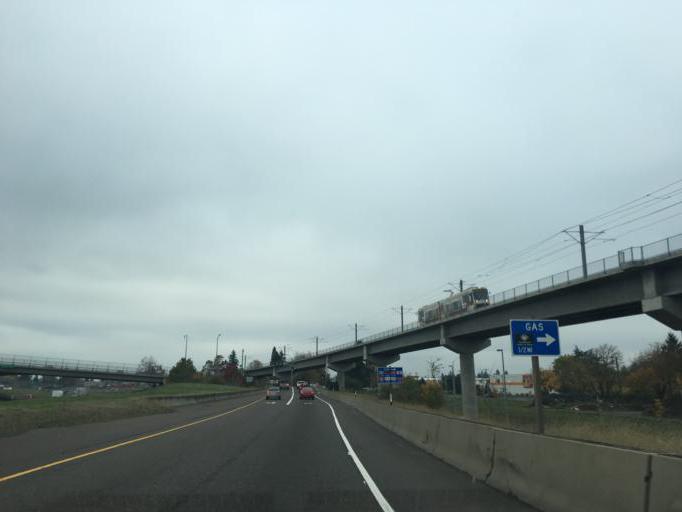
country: US
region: Oregon
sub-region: Multnomah County
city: Lents
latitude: 45.4585
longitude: -122.5731
